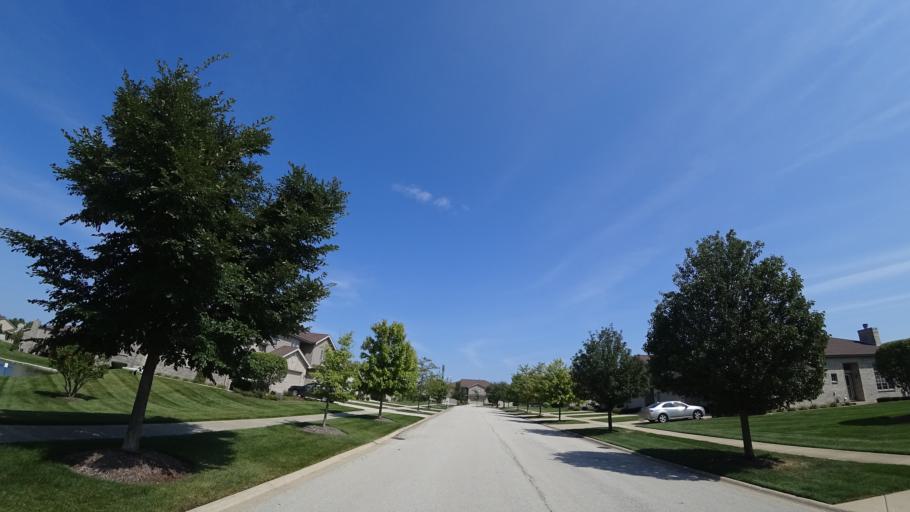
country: US
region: Illinois
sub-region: Cook County
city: Orland Hills
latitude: 41.5600
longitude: -87.8446
